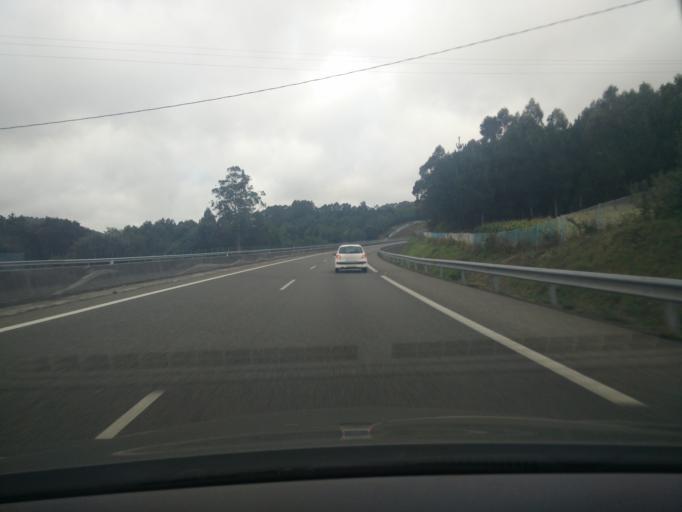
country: ES
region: Galicia
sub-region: Provincia da Coruna
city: Laracha
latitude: 43.2681
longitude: -8.5854
